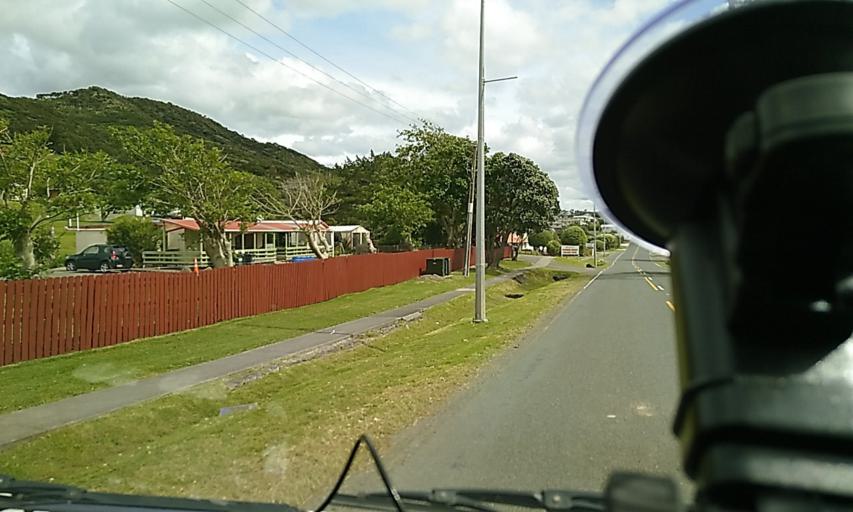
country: NZ
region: Northland
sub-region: Far North District
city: Ahipara
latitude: -35.5079
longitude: 173.3902
